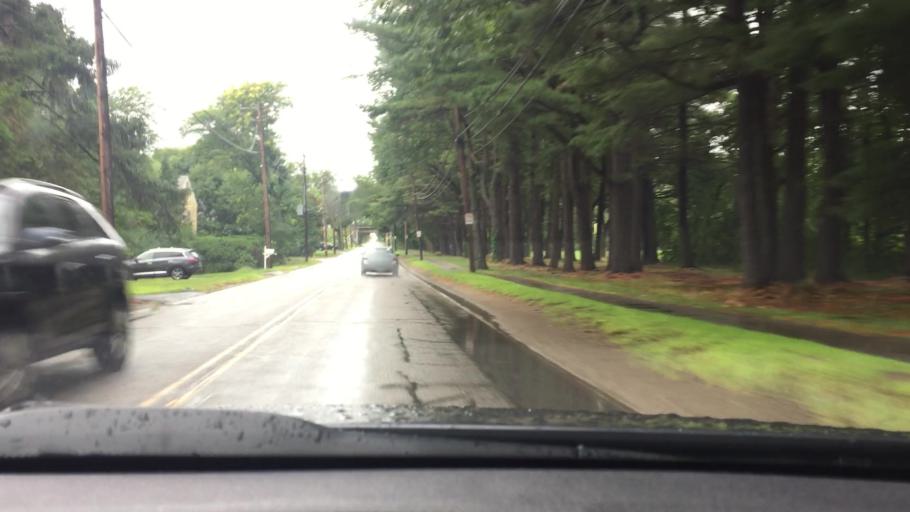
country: US
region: Massachusetts
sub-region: Norfolk County
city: Needham
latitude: 42.2723
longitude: -71.2249
